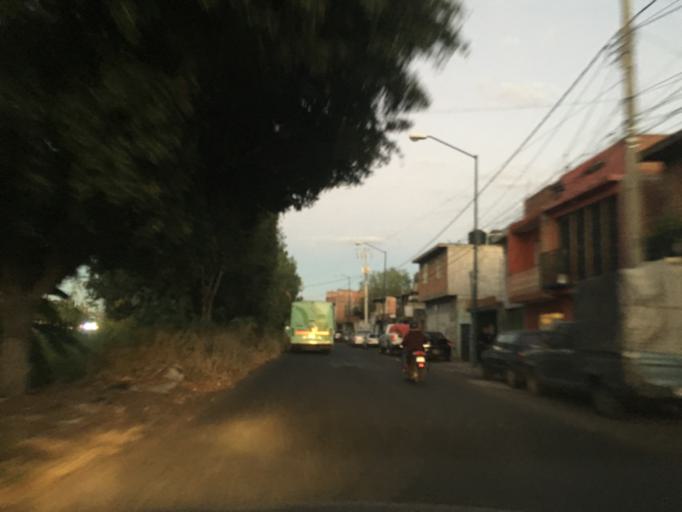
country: MX
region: Michoacan
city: Morelia
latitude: 19.7129
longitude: -101.1871
